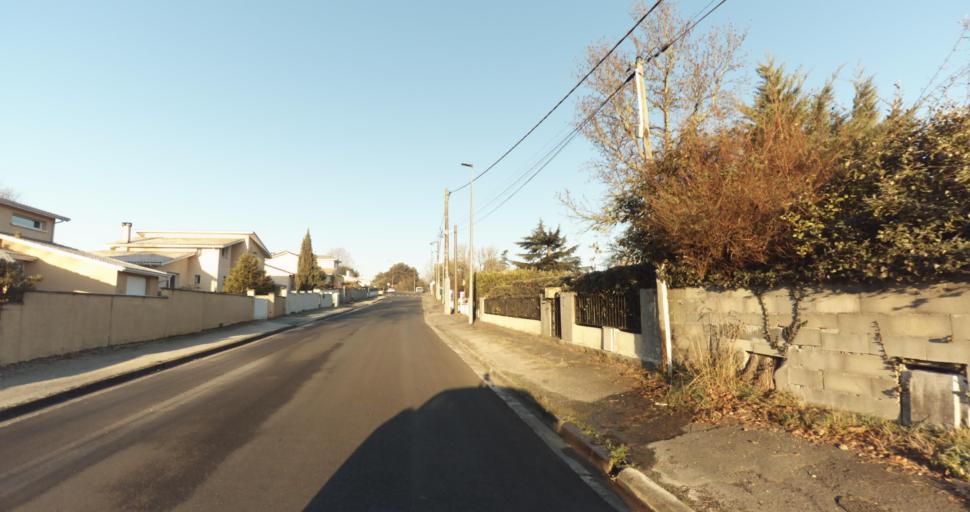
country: FR
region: Aquitaine
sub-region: Departement de la Gironde
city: Carbon-Blanc
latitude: 44.9095
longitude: -0.4981
